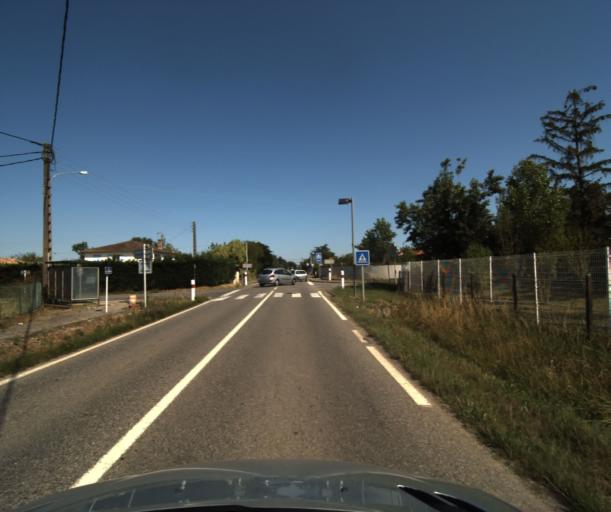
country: FR
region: Midi-Pyrenees
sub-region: Departement de la Haute-Garonne
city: Labarthe-sur-Leze
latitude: 43.4582
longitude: 1.3806
